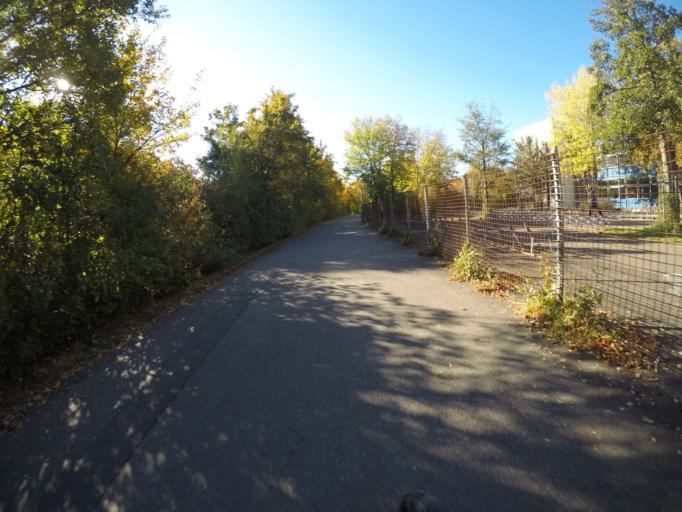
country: DE
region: Baden-Wuerttemberg
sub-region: Regierungsbezirk Stuttgart
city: Filderstadt
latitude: 48.6720
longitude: 9.2138
